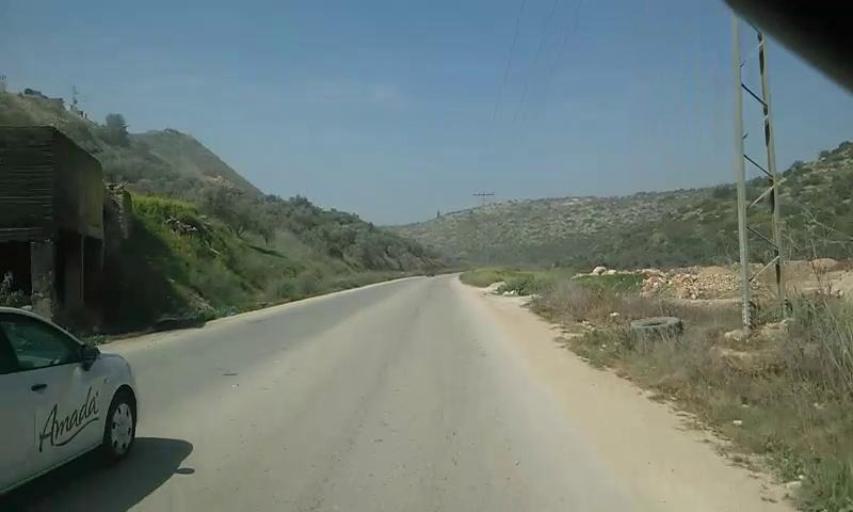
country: PS
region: West Bank
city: Az Zababidah
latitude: 32.4053
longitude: 35.3136
